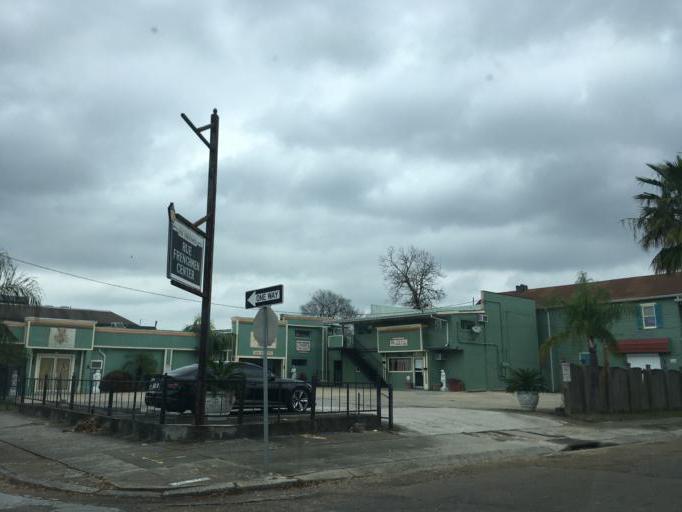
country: US
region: Louisiana
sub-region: Orleans Parish
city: New Orleans
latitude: 29.9968
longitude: -90.0604
